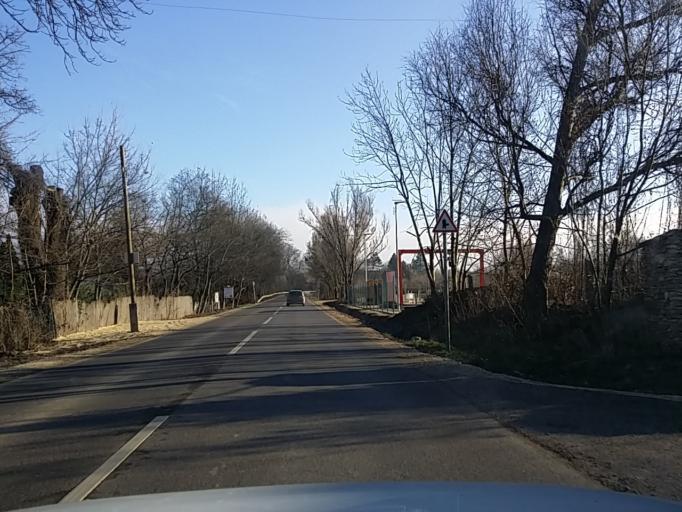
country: HU
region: Pest
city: Solymar
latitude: 47.5572
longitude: 18.9244
